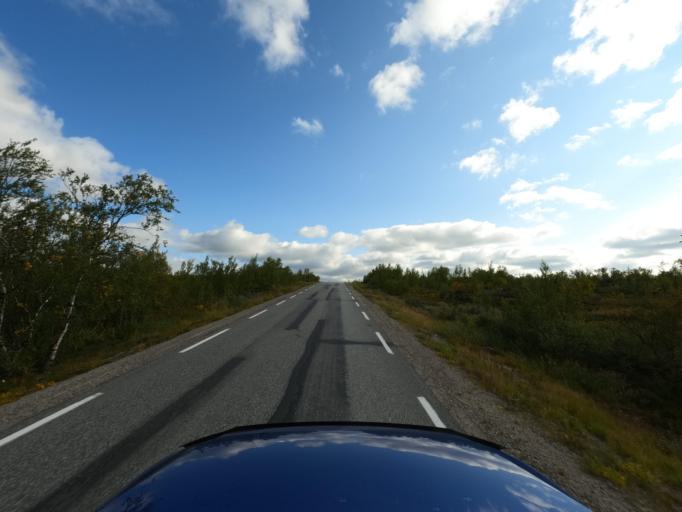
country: NO
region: Finnmark Fylke
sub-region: Porsanger
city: Lakselv
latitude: 69.3909
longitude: 24.5202
